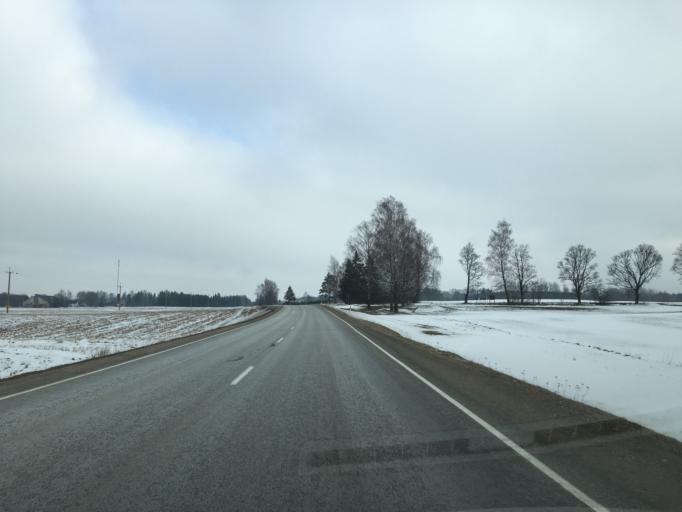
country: EE
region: Tartu
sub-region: Elva linn
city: Elva
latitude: 58.1228
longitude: 26.2426
